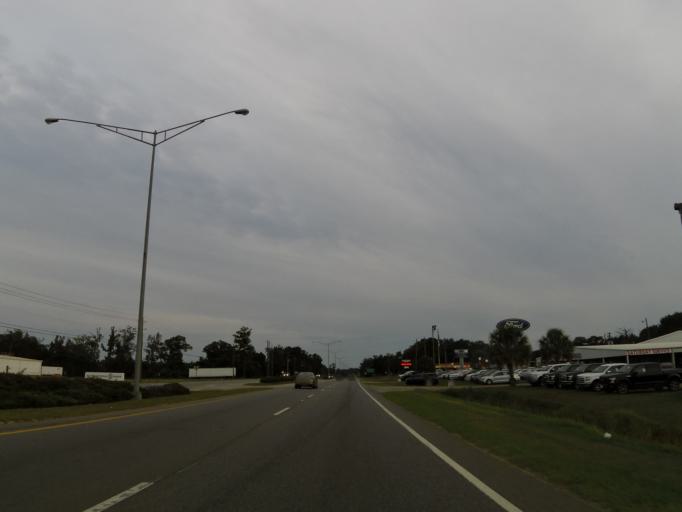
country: US
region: Alabama
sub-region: Baldwin County
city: Bay Minette
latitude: 30.8625
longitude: -87.7767
